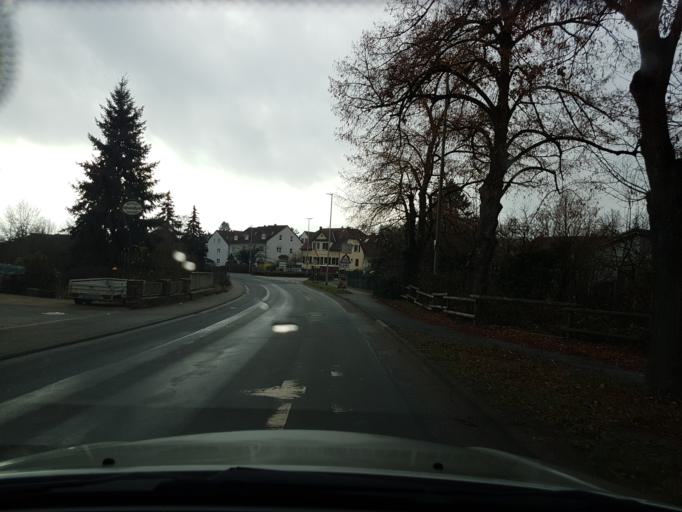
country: DE
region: Hesse
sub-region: Regierungsbezirk Darmstadt
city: Eltville
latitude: 50.0373
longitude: 8.1172
